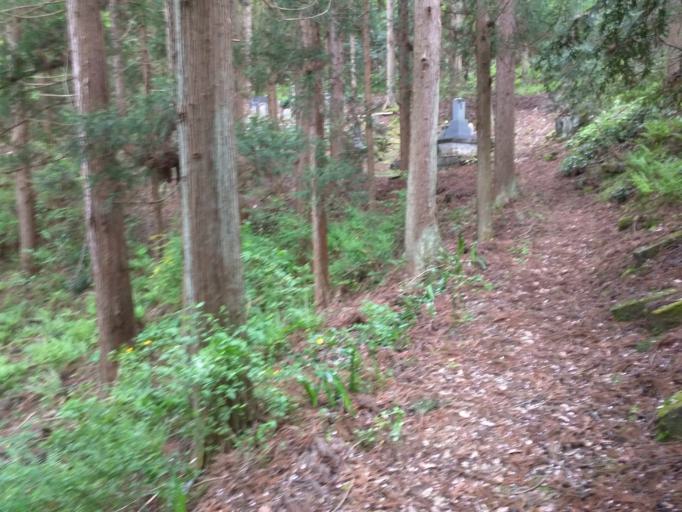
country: JP
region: Fukushima
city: Kitakata
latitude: 37.4340
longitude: 139.8896
